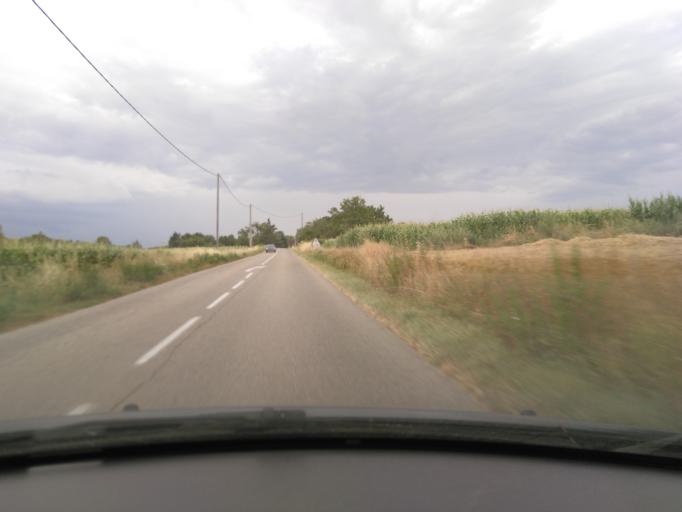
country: FR
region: Rhone-Alpes
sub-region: Departement de l'Isere
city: Beaurepaire
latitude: 45.3834
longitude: 5.0182
